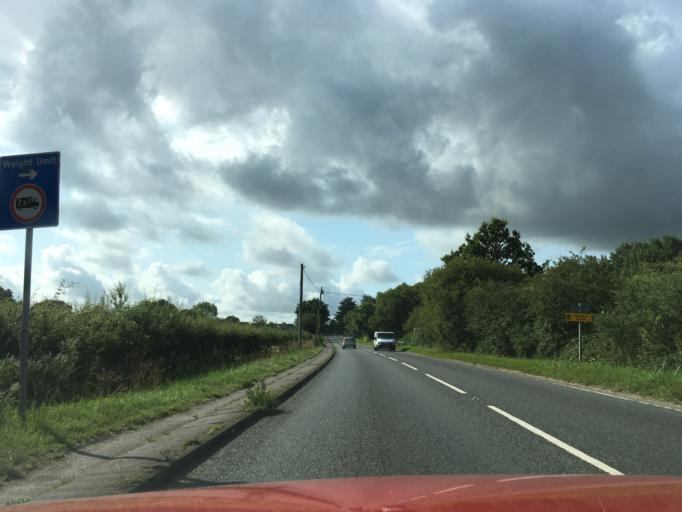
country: GB
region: England
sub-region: Hampshire
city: Bishops Waltham
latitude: 50.9418
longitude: -1.2027
